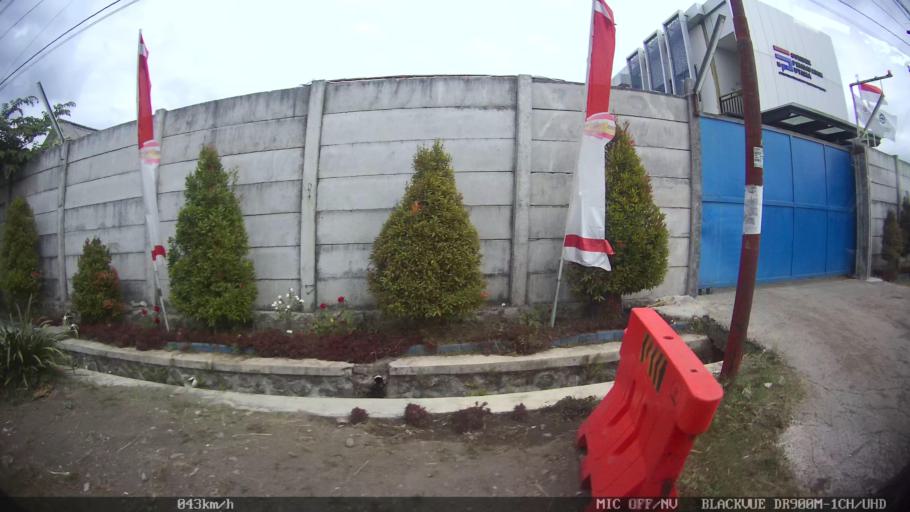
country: ID
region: Daerah Istimewa Yogyakarta
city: Depok
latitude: -7.8197
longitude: 110.4426
